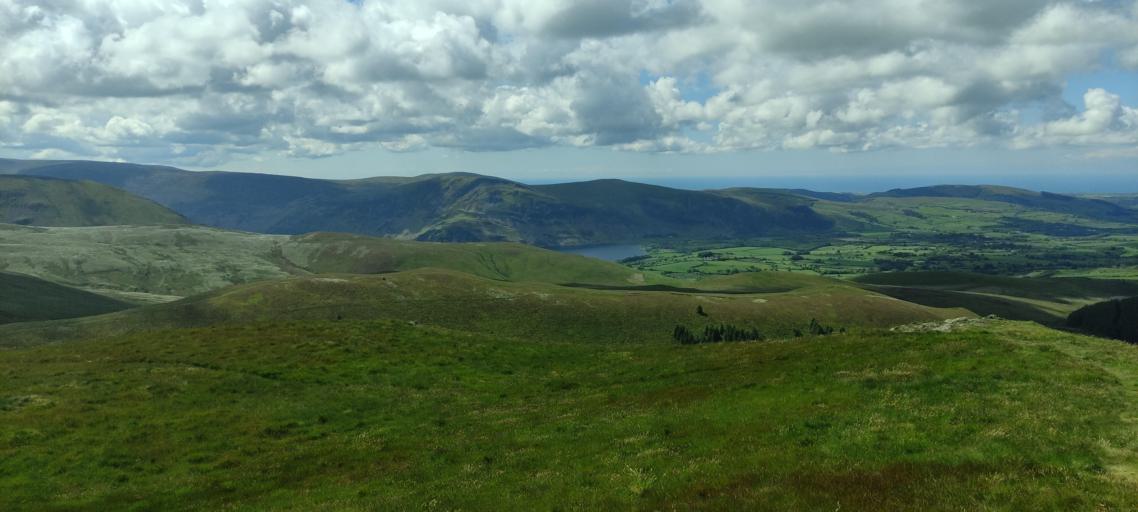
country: GB
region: England
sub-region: Cumbria
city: Cockermouth
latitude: 54.5645
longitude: -3.3772
